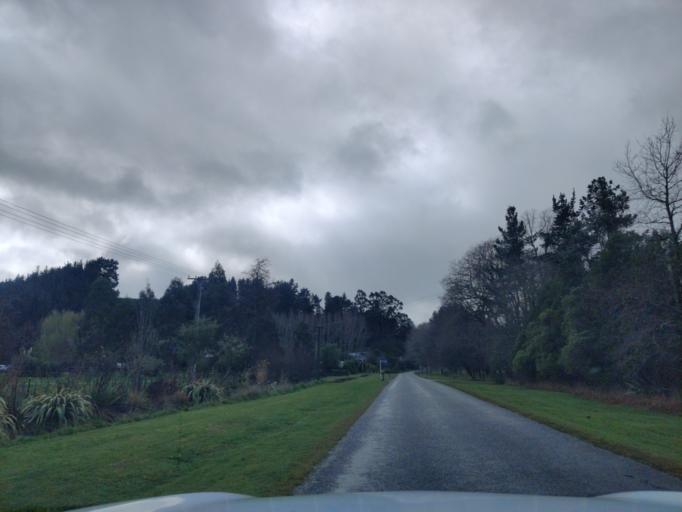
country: NZ
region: Manawatu-Wanganui
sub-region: Palmerston North City
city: Palmerston North
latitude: -40.1695
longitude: 175.8001
